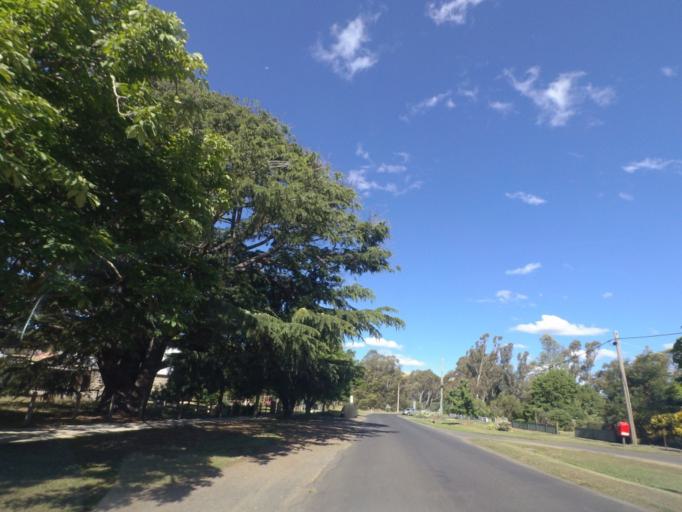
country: AU
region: Victoria
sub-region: Hume
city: Craigieburn
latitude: -37.4014
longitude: 144.8931
